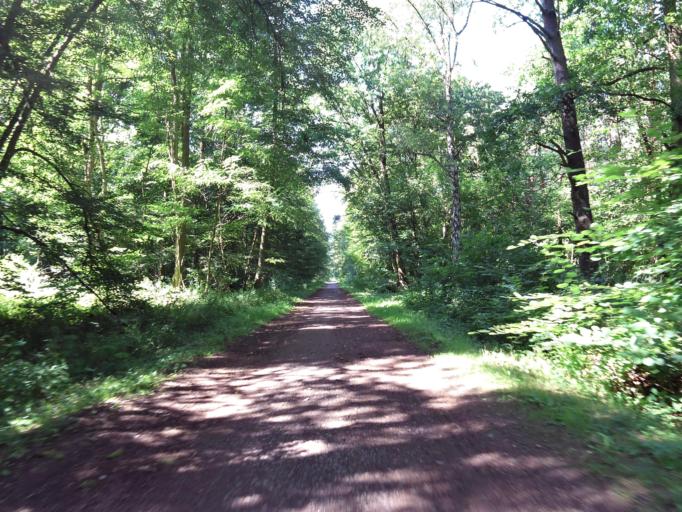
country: DE
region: Rheinland-Pfalz
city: Hanhofen
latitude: 49.3359
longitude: 8.3342
